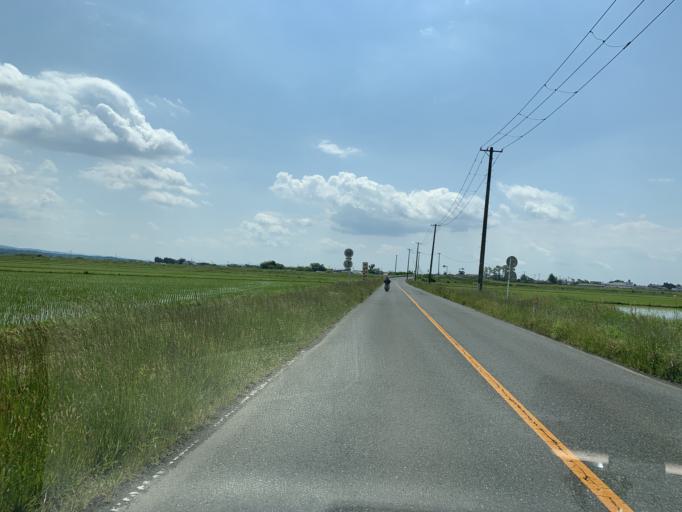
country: JP
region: Miyagi
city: Kogota
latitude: 38.5916
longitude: 141.0295
